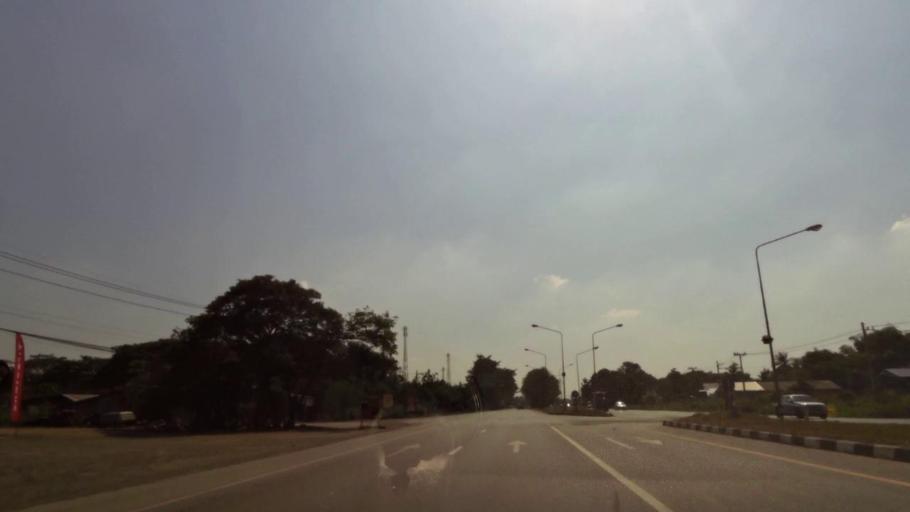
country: TH
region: Phichit
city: Bueng Na Rang
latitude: 16.1938
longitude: 100.1285
